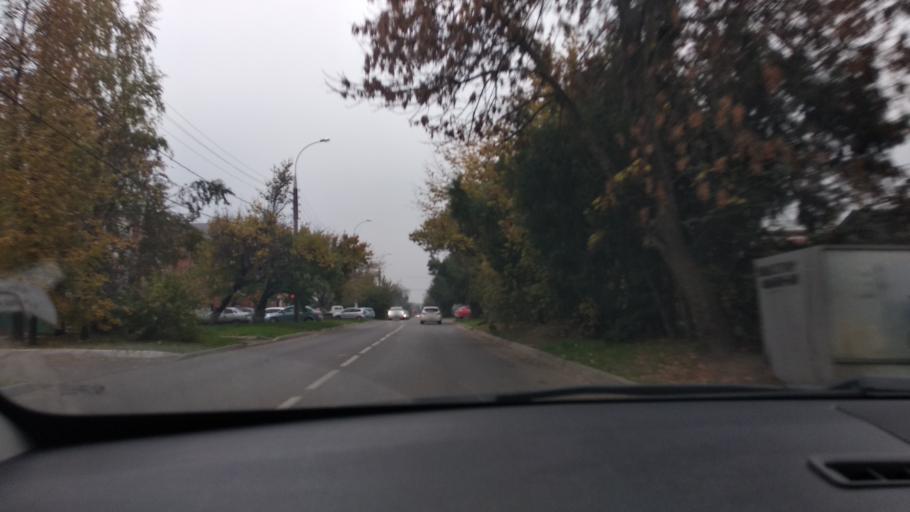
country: RU
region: Krasnodarskiy
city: Krasnodar
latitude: 45.0194
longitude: 39.0101
